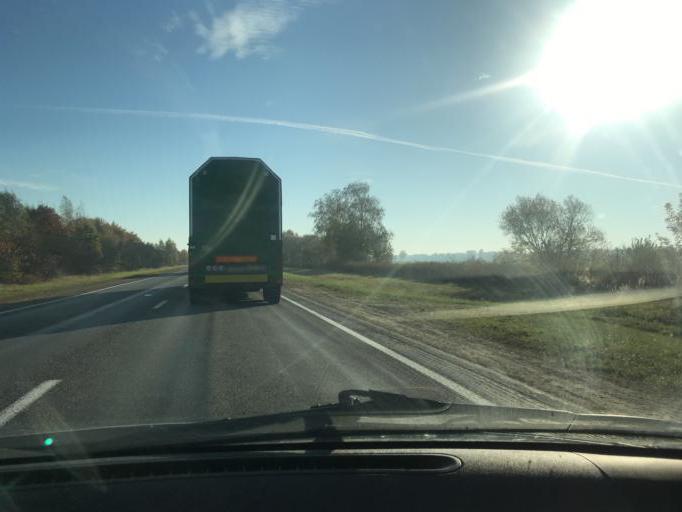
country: BY
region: Brest
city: Ivanava
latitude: 52.1486
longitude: 25.4142
